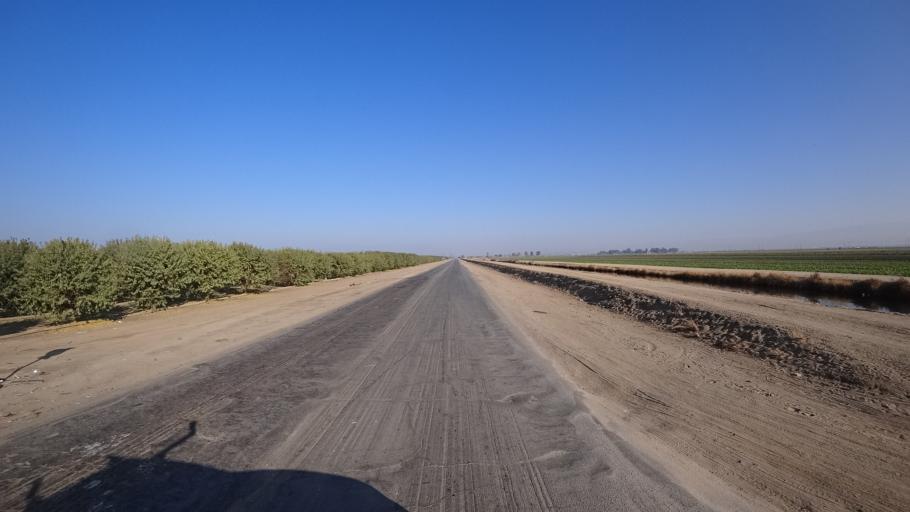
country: US
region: California
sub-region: Kern County
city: Greenfield
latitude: 35.2524
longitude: -118.9853
